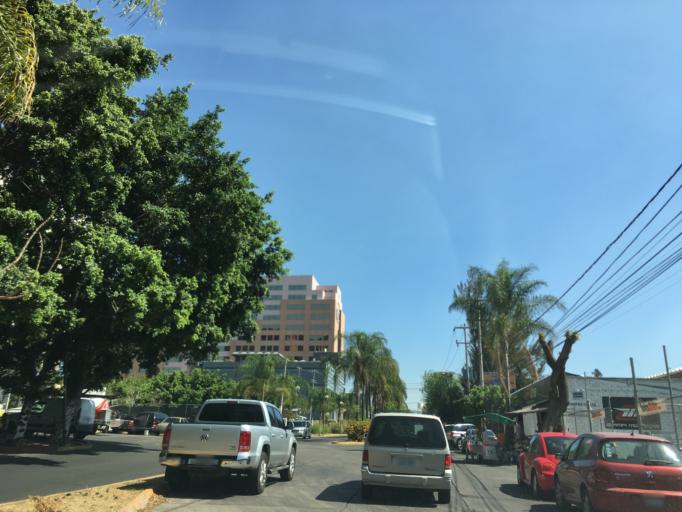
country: MX
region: Jalisco
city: Guadalajara
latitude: 20.6535
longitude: -103.3889
